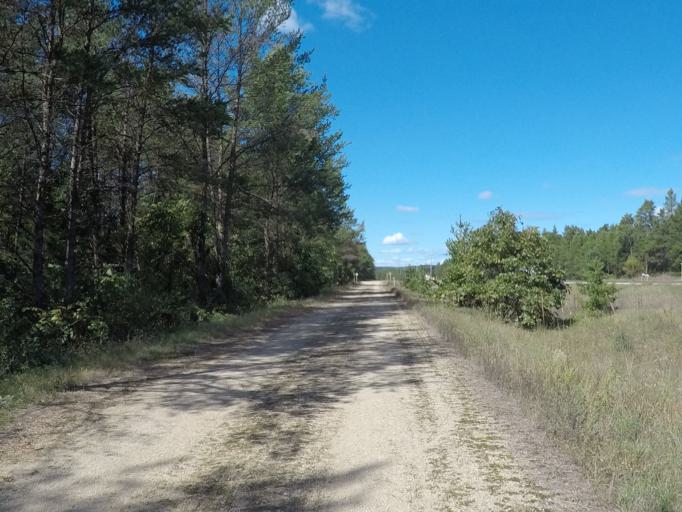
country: US
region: Wisconsin
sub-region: Richland County
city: Richland Center
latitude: 43.2143
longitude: -90.2805
